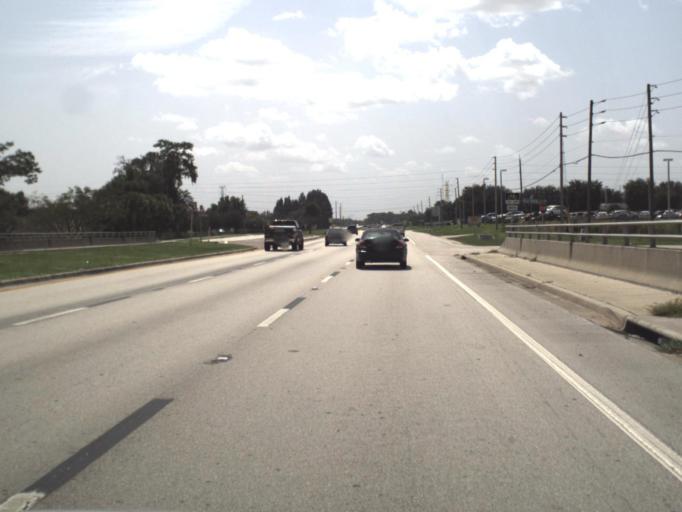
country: US
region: Florida
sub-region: Highlands County
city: Avon Park
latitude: 27.5801
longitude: -81.5146
